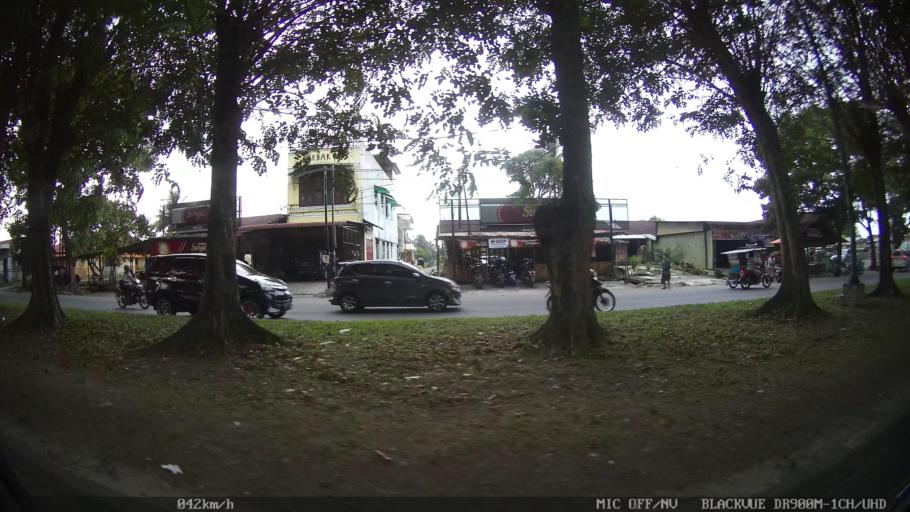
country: ID
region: North Sumatra
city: Sunggal
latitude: 3.5406
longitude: 98.6410
